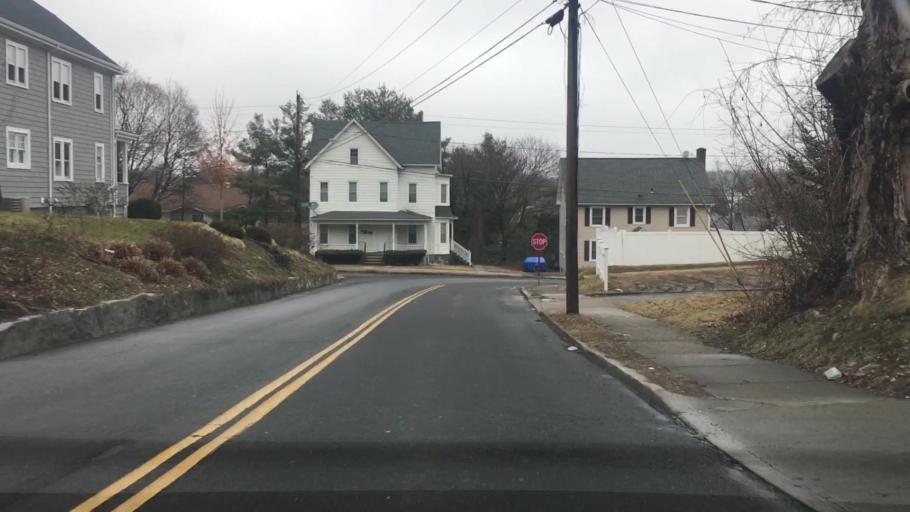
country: US
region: Connecticut
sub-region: Fairfield County
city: Danbury
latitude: 41.3851
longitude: -73.4478
